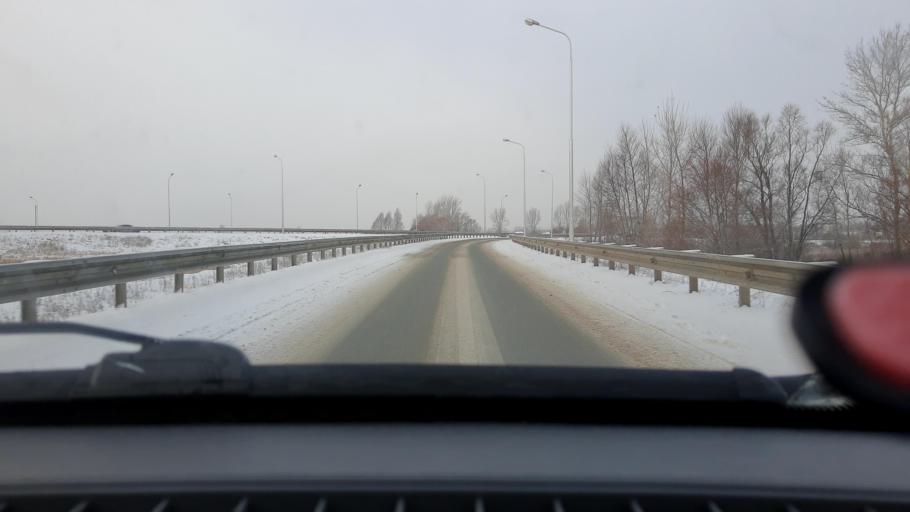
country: RU
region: Bashkortostan
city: Kabakovo
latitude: 54.6525
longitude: 56.0848
